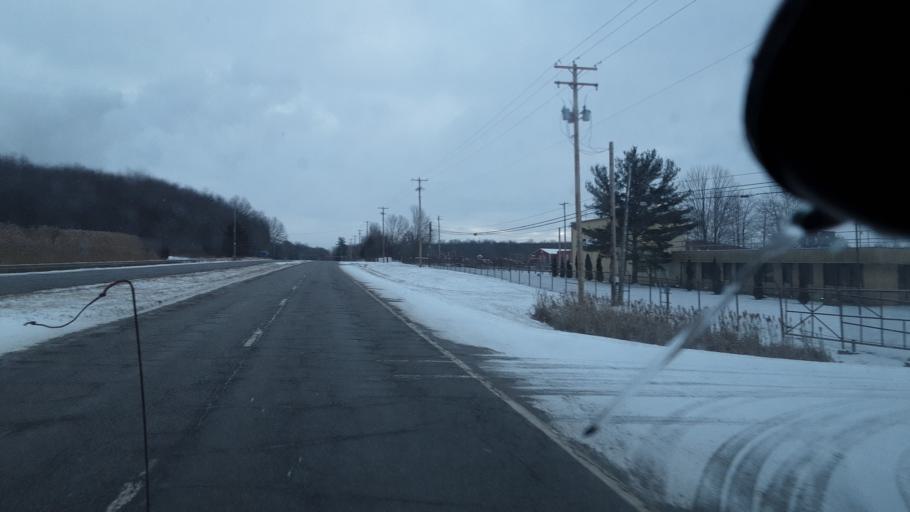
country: US
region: Ohio
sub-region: Trumbull County
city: Lordstown
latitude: 41.1437
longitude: -80.8641
